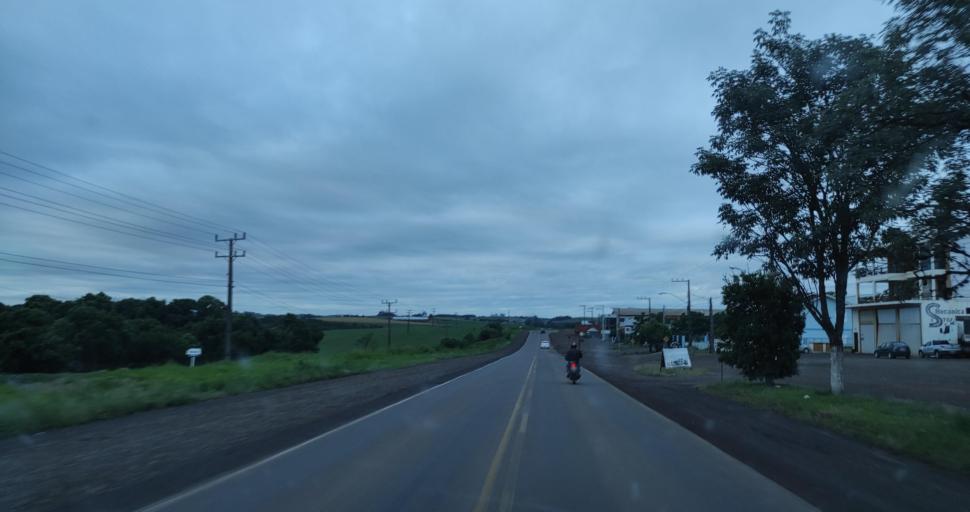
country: BR
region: Santa Catarina
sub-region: Xanxere
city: Xanxere
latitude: -26.7414
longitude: -52.3954
